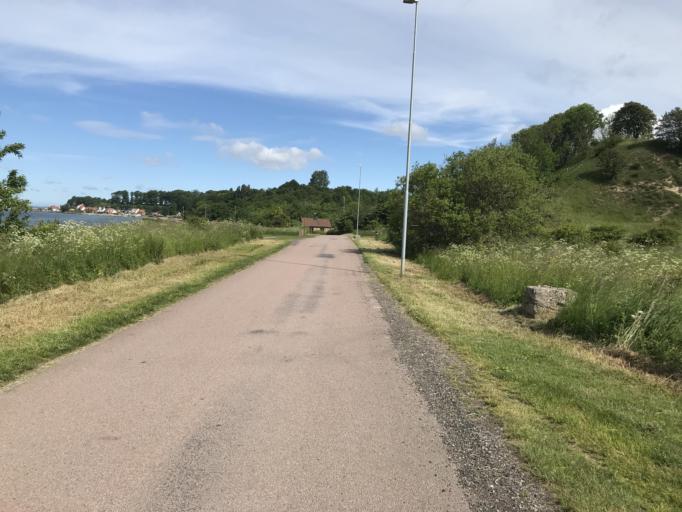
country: SE
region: Skane
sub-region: Helsingborg
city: Glumslov
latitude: 55.9333
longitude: 12.7875
